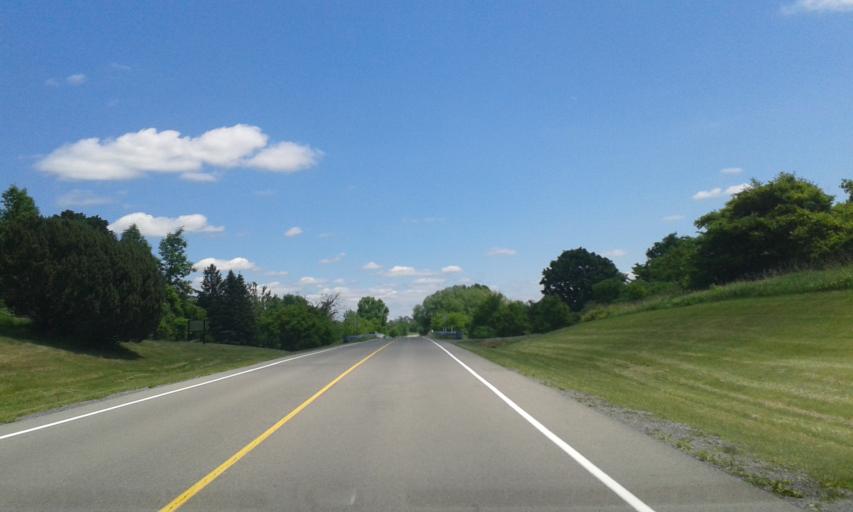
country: US
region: New York
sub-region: St. Lawrence County
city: Massena
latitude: 44.9957
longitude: -74.9231
